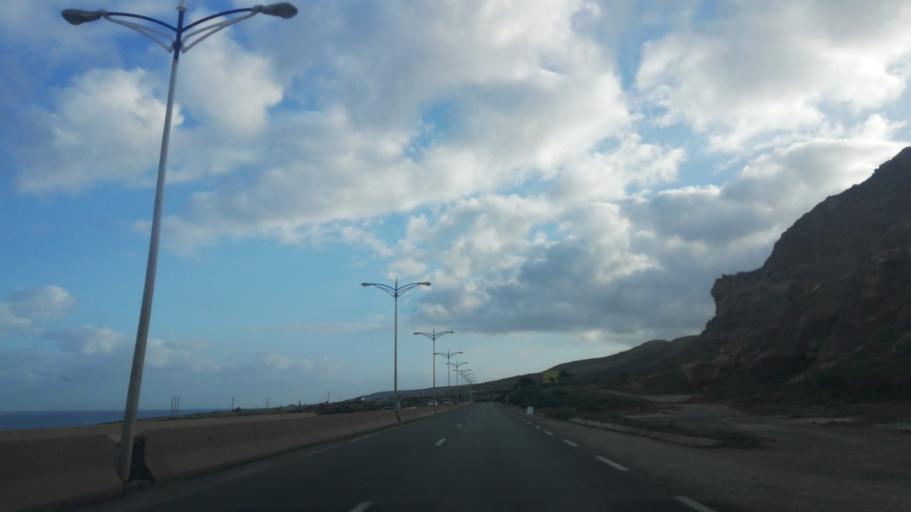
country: DZ
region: Mostaganem
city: Mostaganem
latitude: 36.0555
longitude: 0.1602
